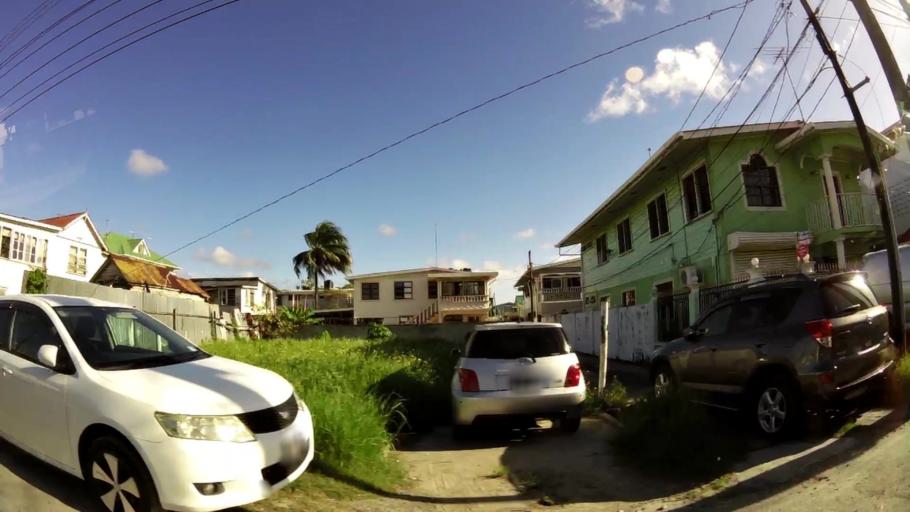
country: GY
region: Demerara-Mahaica
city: Georgetown
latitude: 6.8171
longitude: -58.1410
